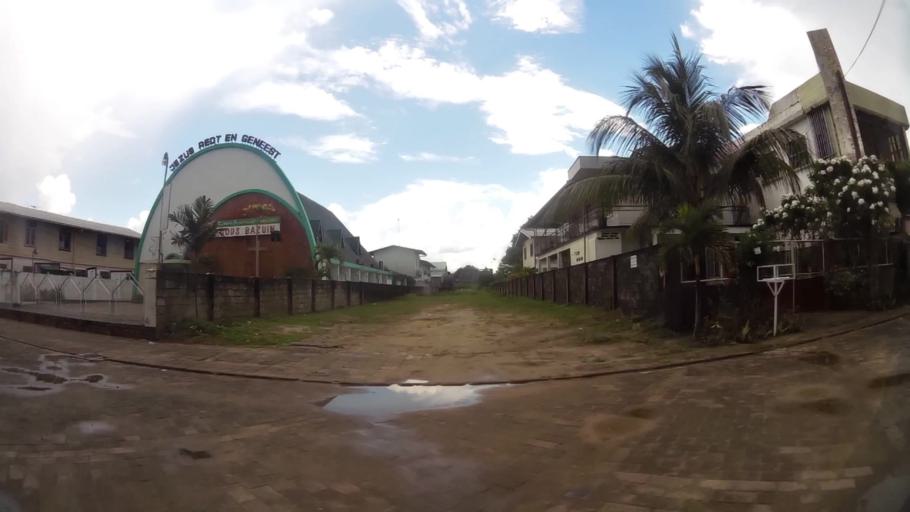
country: SR
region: Paramaribo
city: Paramaribo
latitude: 5.8338
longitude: -55.1696
